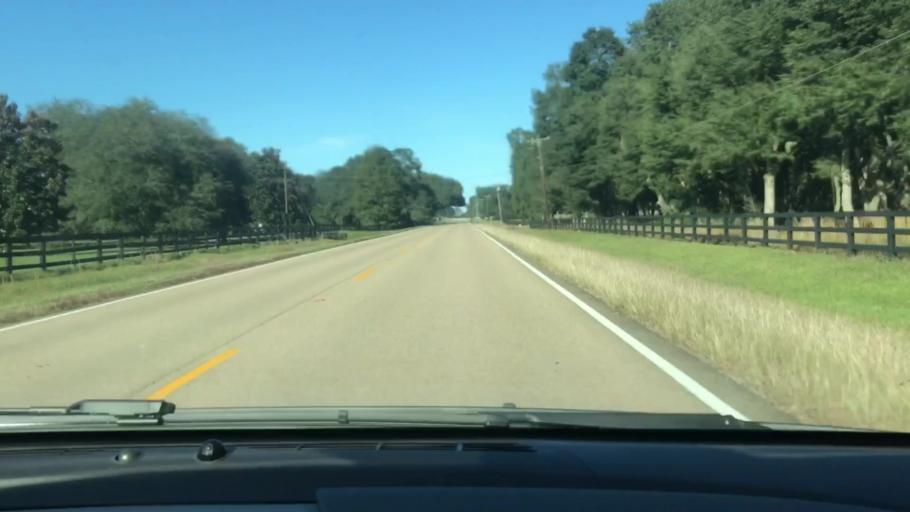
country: US
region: Louisiana
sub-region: Saint Tammany Parish
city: Abita Springs
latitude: 30.5910
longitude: -90.0323
